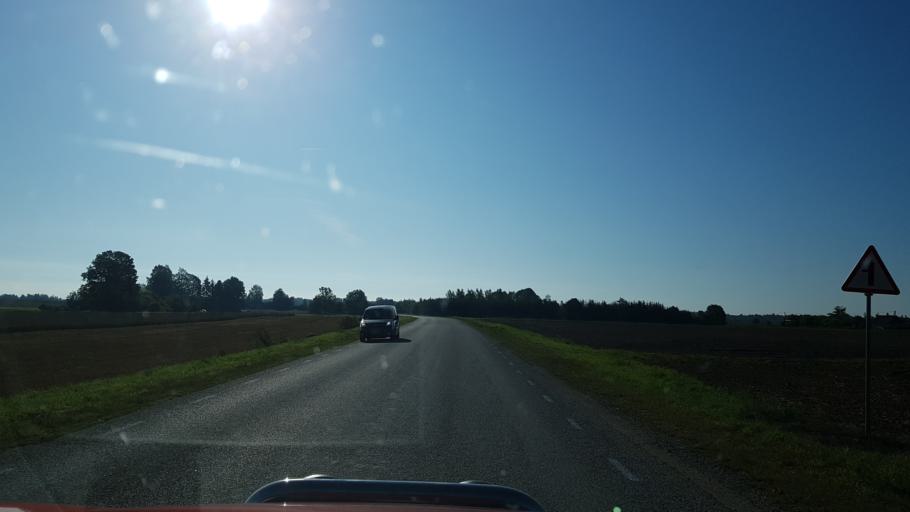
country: EE
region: Jogevamaa
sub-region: Tabivere vald
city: Tabivere
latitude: 58.6774
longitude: 26.6690
